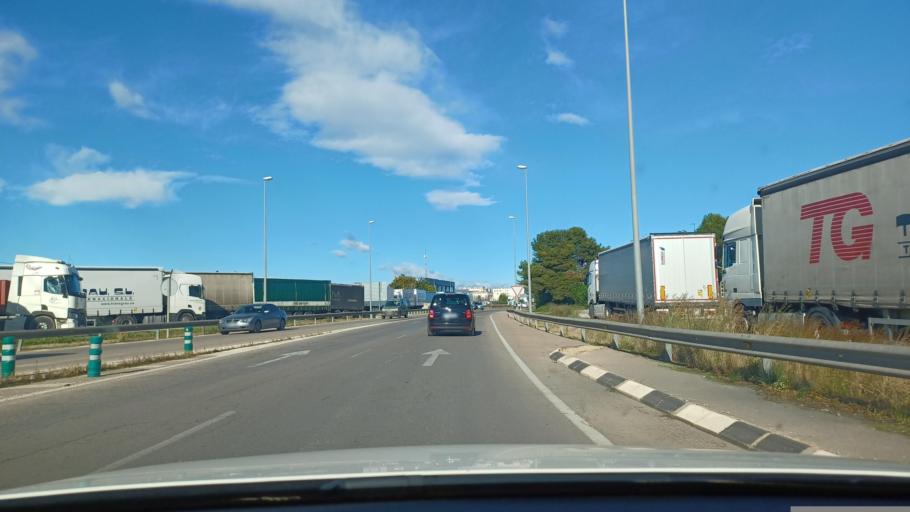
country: ES
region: Valencia
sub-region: Provincia de Castello
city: Vinaros
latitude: 40.4714
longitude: 0.4652
